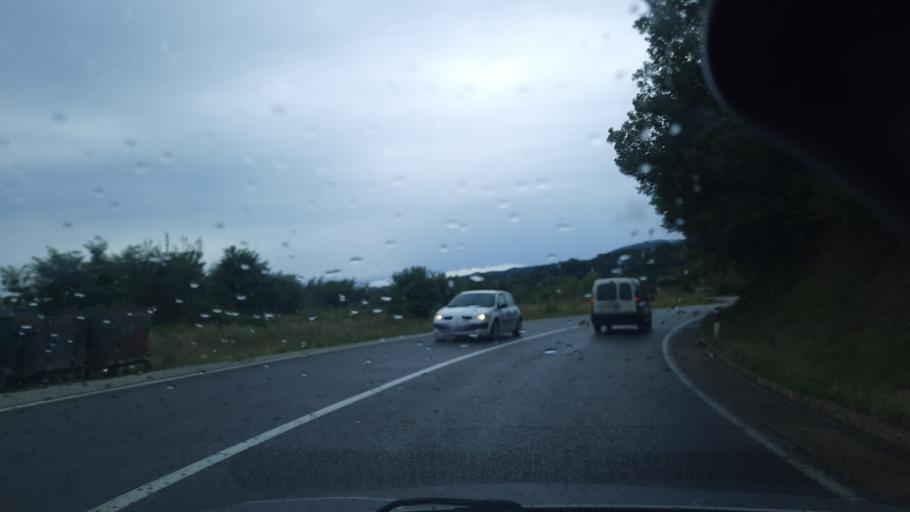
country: RS
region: Central Serbia
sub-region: Raski Okrug
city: Kraljevo
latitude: 43.8046
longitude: 20.7875
